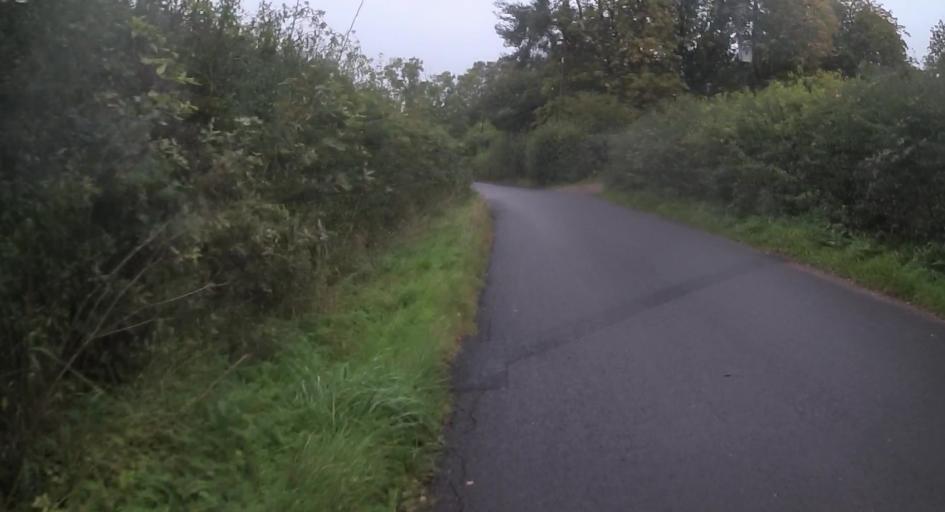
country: GB
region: England
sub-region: West Berkshire
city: Thatcham
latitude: 51.4128
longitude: -1.2134
